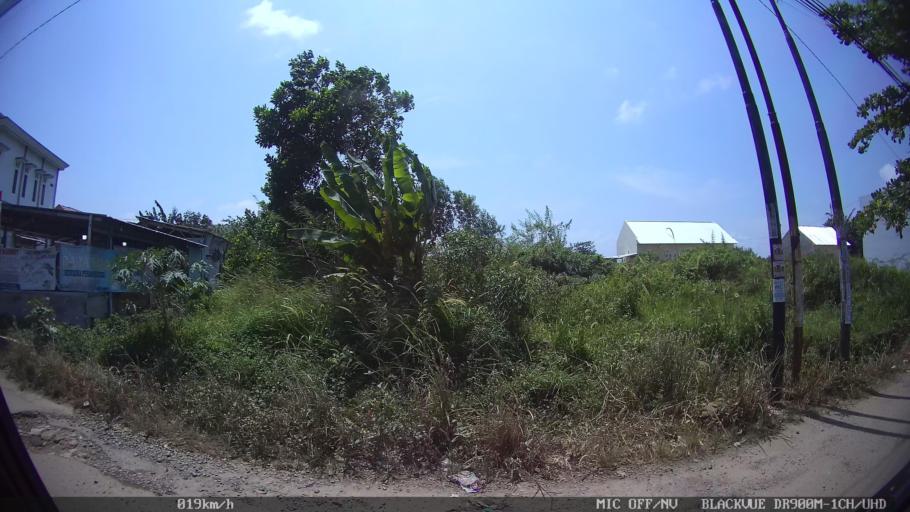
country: ID
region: Lampung
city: Kedaton
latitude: -5.3617
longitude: 105.2747
